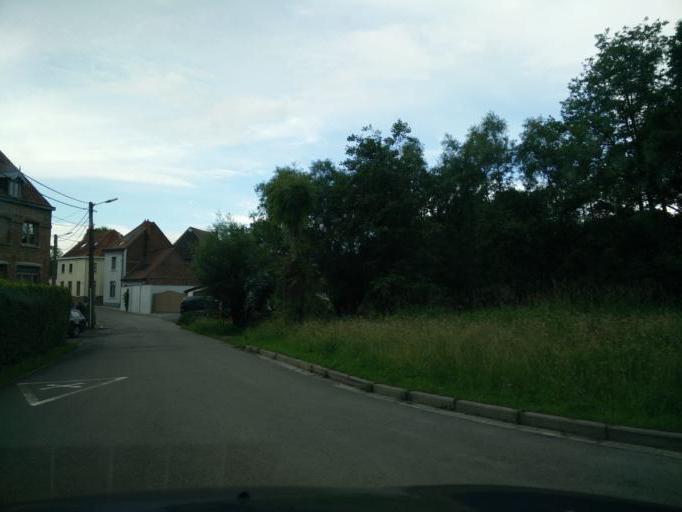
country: BE
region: Flanders
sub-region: Provincie Vlaams-Brabant
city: Beersel
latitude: 50.7201
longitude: 4.3104
